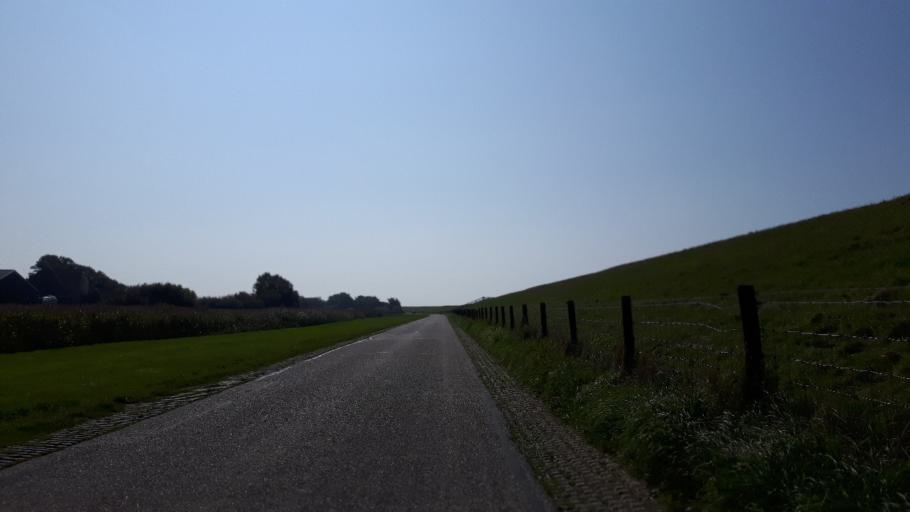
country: NL
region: Friesland
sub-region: Sudwest Fryslan
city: Makkum
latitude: 53.0875
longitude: 5.3820
